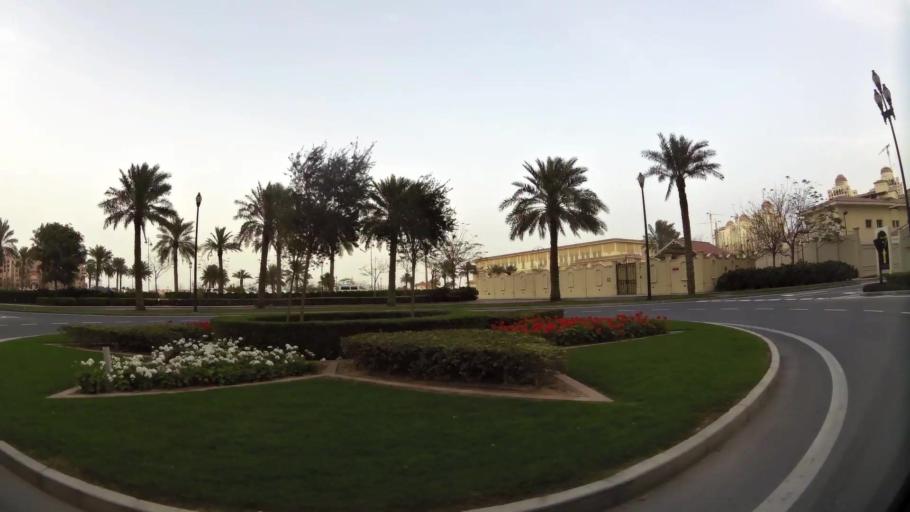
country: QA
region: Baladiyat ad Dawhah
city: Doha
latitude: 25.3713
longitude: 51.5492
